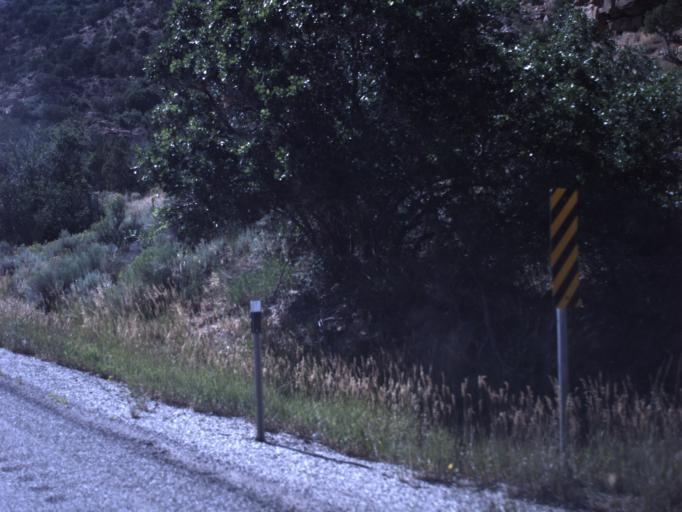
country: US
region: Utah
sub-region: Duchesne County
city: Duchesne
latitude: 40.1994
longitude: -110.9144
